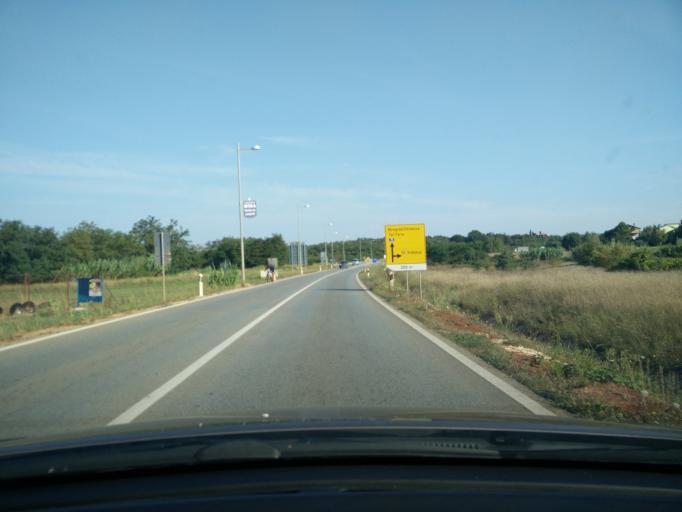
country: HR
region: Istarska
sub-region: Grad Porec
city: Porec
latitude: 45.2611
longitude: 13.6125
